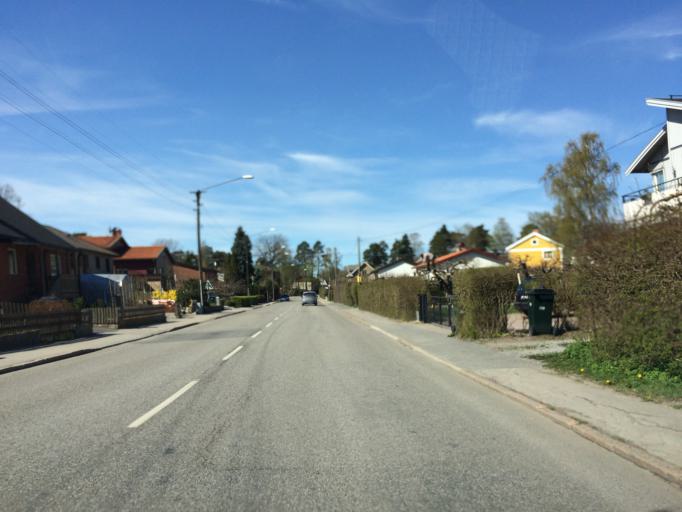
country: SE
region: Stockholm
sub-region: Huddinge Kommun
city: Huddinge
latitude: 59.2669
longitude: 17.9761
